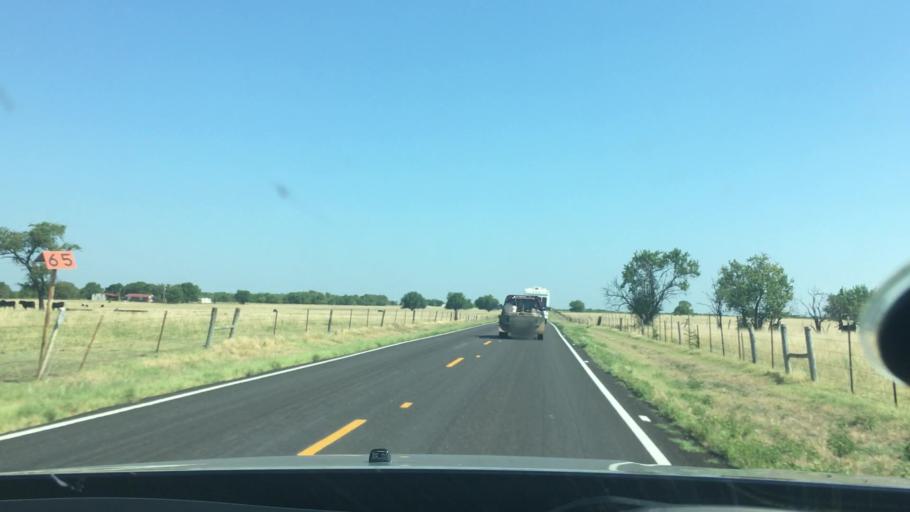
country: US
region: Oklahoma
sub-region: Johnston County
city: Tishomingo
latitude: 34.1751
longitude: -96.5108
